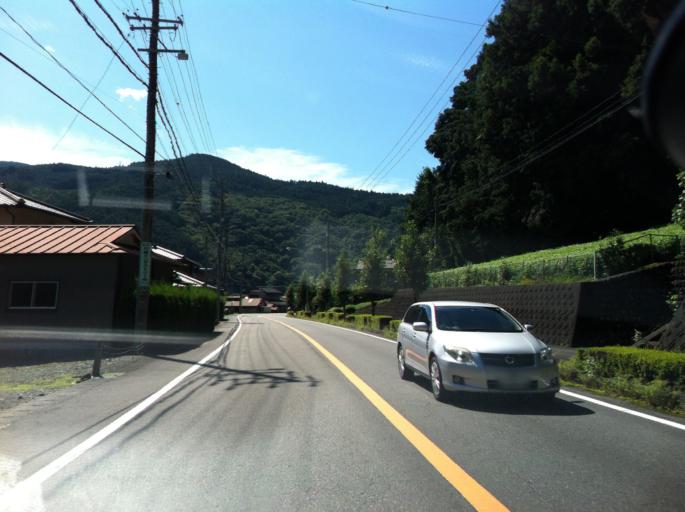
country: JP
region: Shizuoka
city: Fujieda
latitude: 35.0946
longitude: 138.1275
